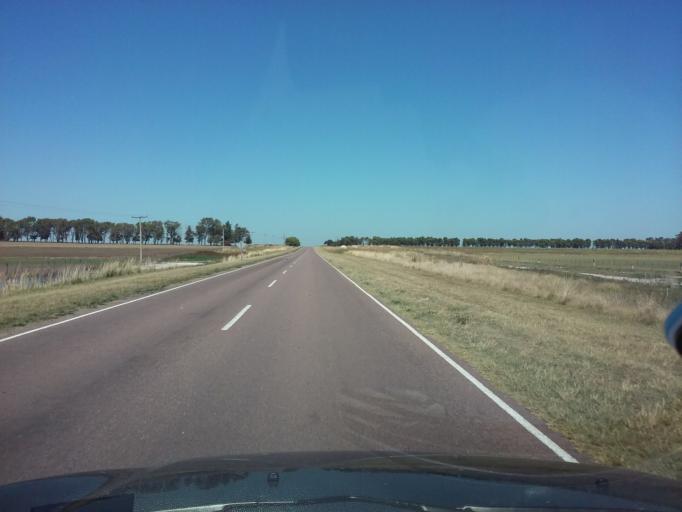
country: AR
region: La Pampa
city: Colonia Baron
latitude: -36.0273
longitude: -63.9413
